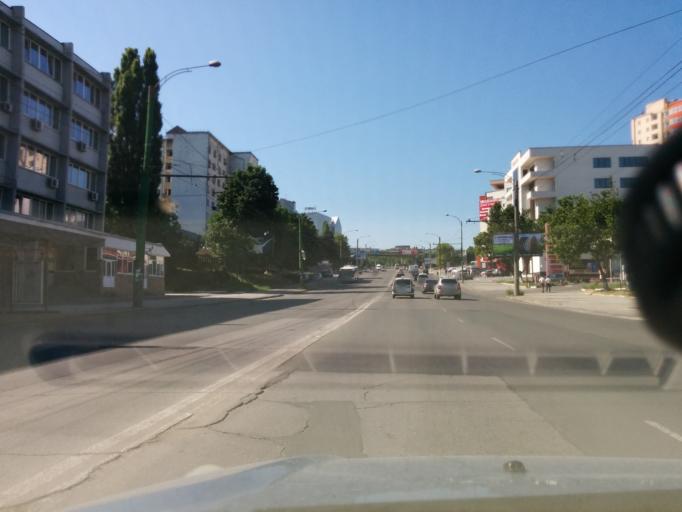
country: MD
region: Chisinau
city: Chisinau
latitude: 47.0077
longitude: 28.8600
